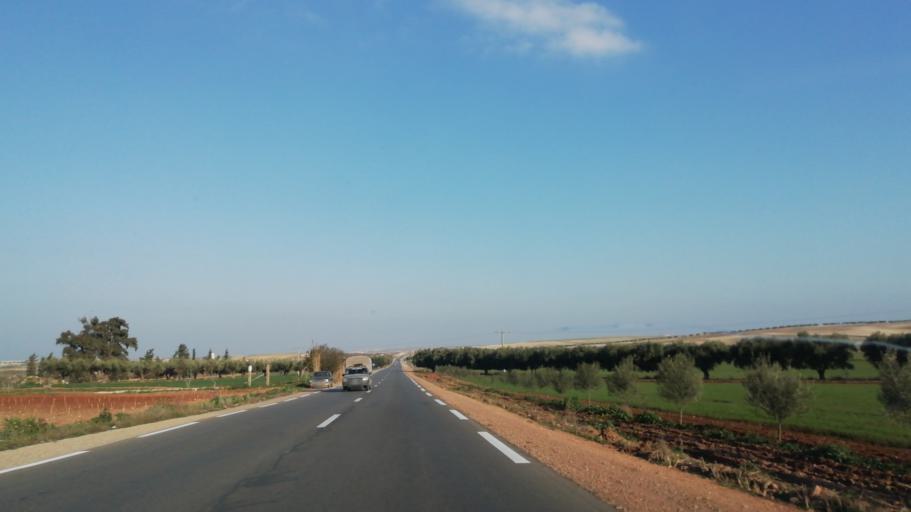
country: DZ
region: Sidi Bel Abbes
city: Sidi Bel Abbes
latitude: 35.1753
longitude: -0.8227
